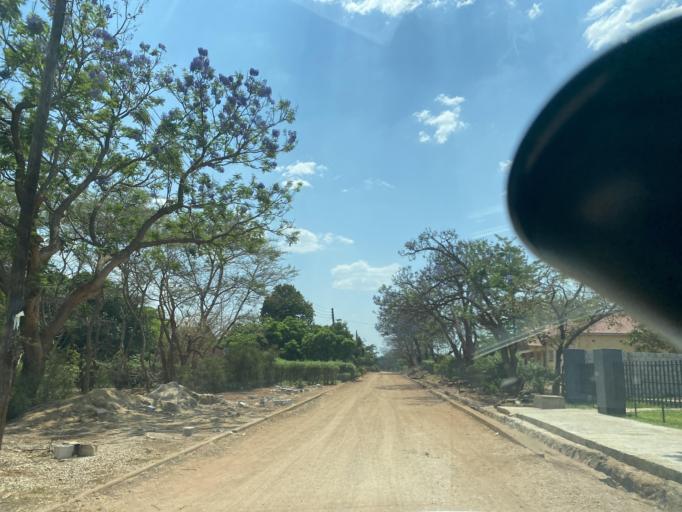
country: ZM
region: Lusaka
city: Kafue
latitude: -15.5064
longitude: 27.9368
